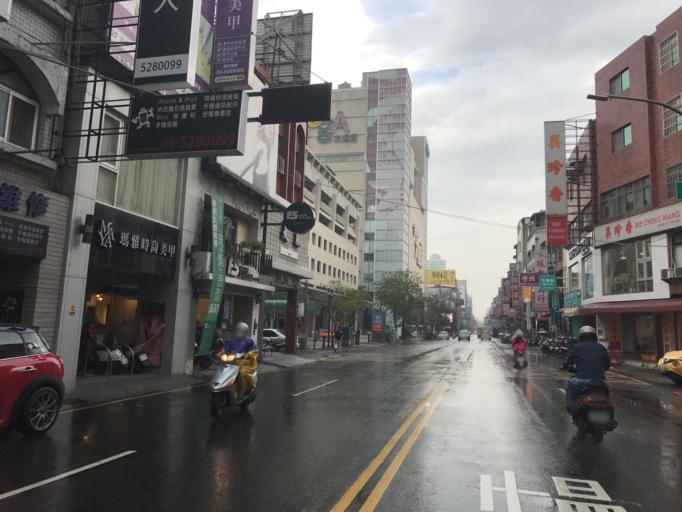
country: TW
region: Taiwan
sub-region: Hsinchu
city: Hsinchu
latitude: 24.8013
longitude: 120.9662
